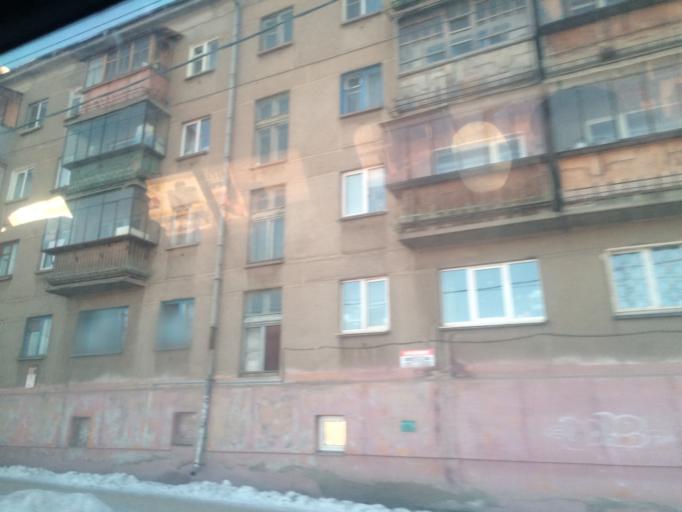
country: RU
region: Chelyabinsk
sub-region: Gorod Magnitogorsk
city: Magnitogorsk
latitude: 53.4372
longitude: 58.9743
